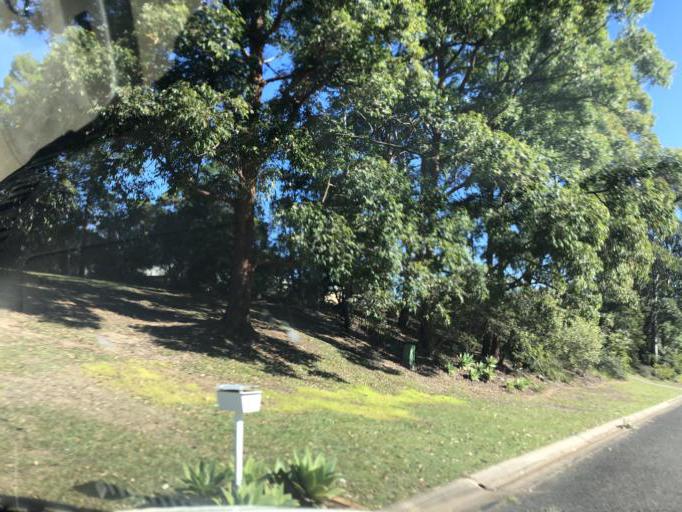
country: AU
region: New South Wales
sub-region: Nambucca Shire
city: Macksville
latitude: -30.6790
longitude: 152.9594
